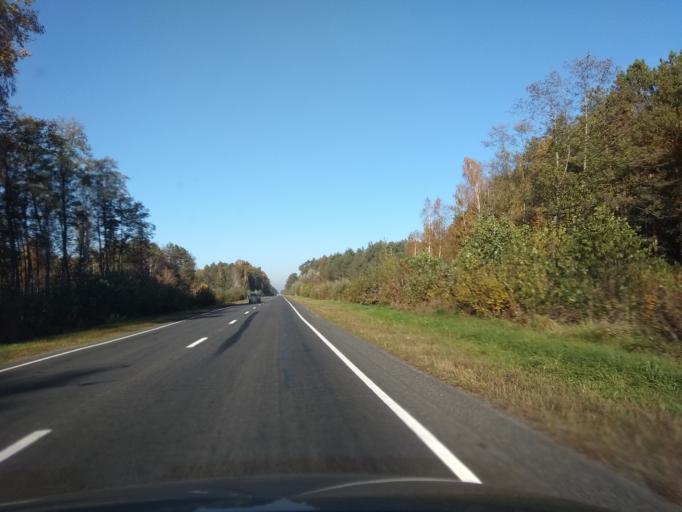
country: BY
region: Brest
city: Malaryta
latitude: 51.9065
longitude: 24.1111
